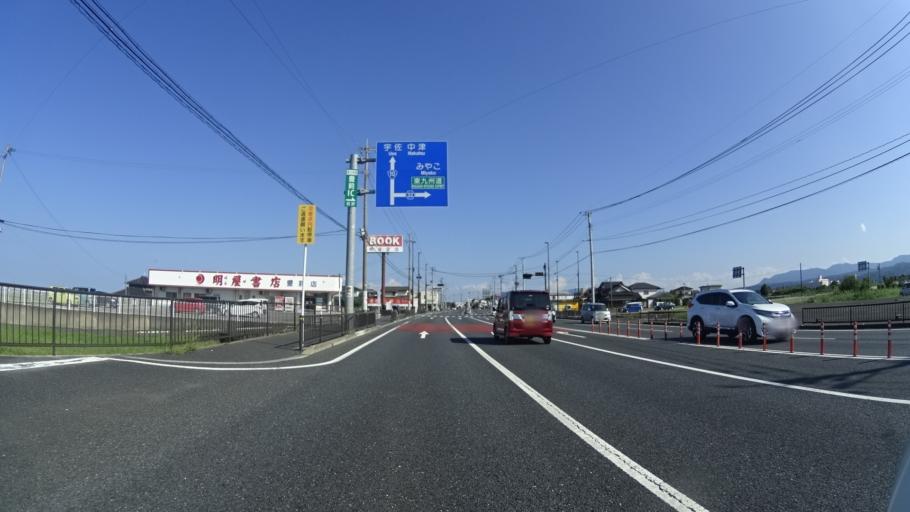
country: JP
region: Fukuoka
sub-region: Buzen-shi
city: Buzen
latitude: 33.6001
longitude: 131.1303
